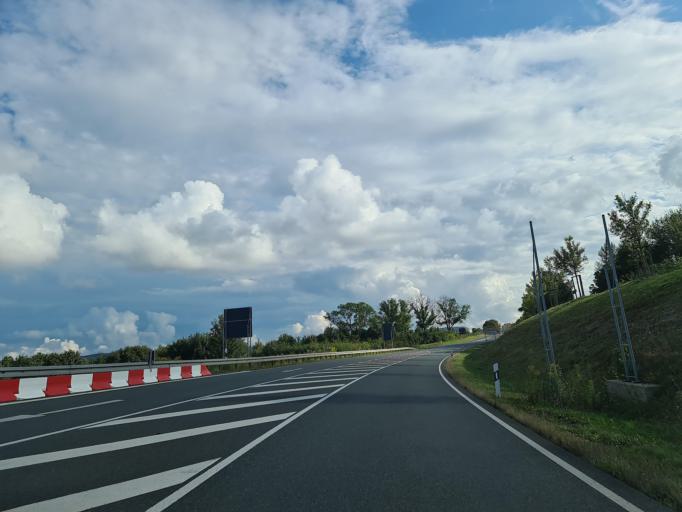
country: DE
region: Saxony
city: Auerbach
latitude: 50.5243
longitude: 12.3817
